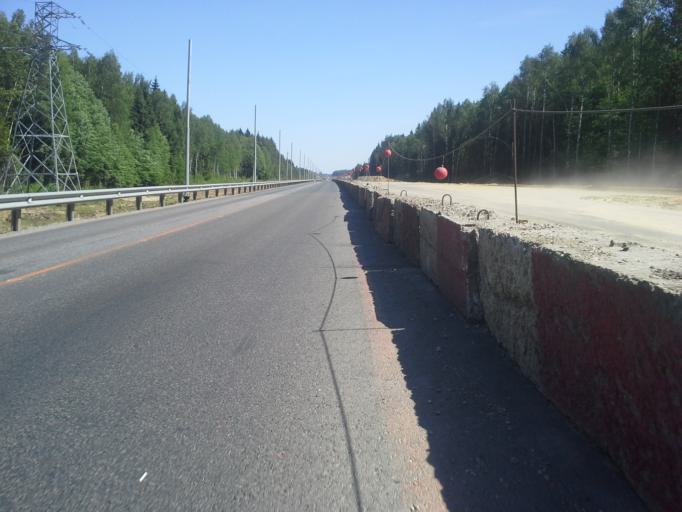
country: RU
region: Moskovskaya
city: Aprelevka
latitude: 55.4674
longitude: 37.0849
